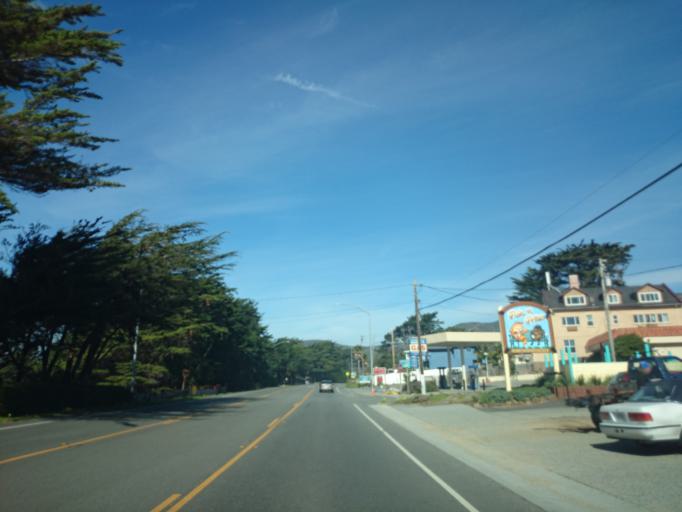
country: US
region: California
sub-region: San Mateo County
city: Montara
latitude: 37.5412
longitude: -122.5163
